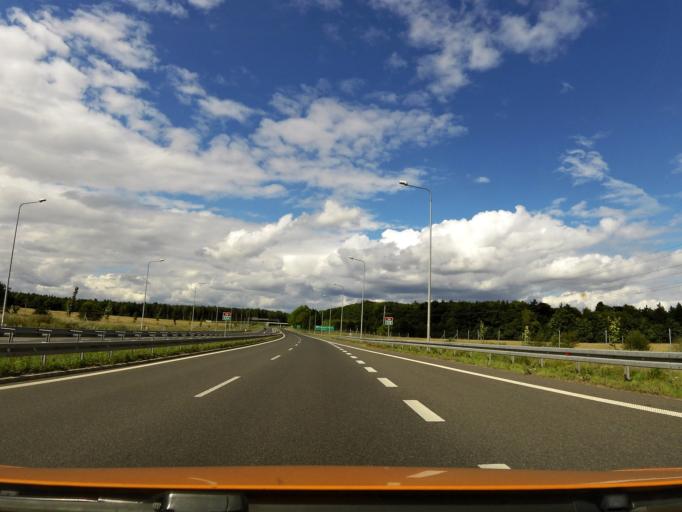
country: PL
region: West Pomeranian Voivodeship
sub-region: Powiat goleniowski
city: Nowogard
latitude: 53.6582
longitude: 15.0784
